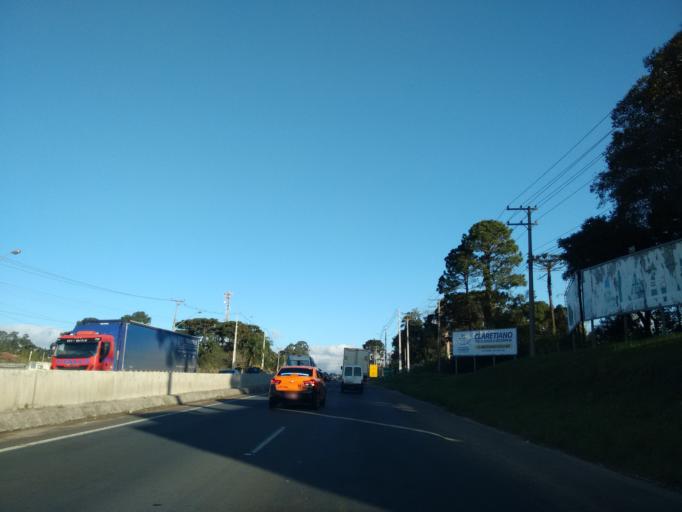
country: BR
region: Parana
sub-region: Sao Jose Dos Pinhais
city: Sao Jose dos Pinhais
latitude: -25.5632
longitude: -49.1838
